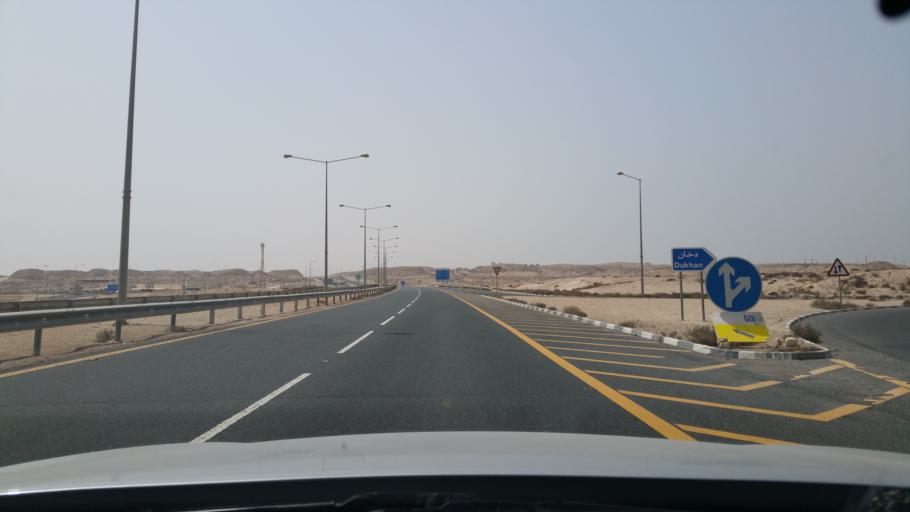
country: QA
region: Baladiyat ar Rayyan
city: Dukhan
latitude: 25.3381
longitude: 50.7833
